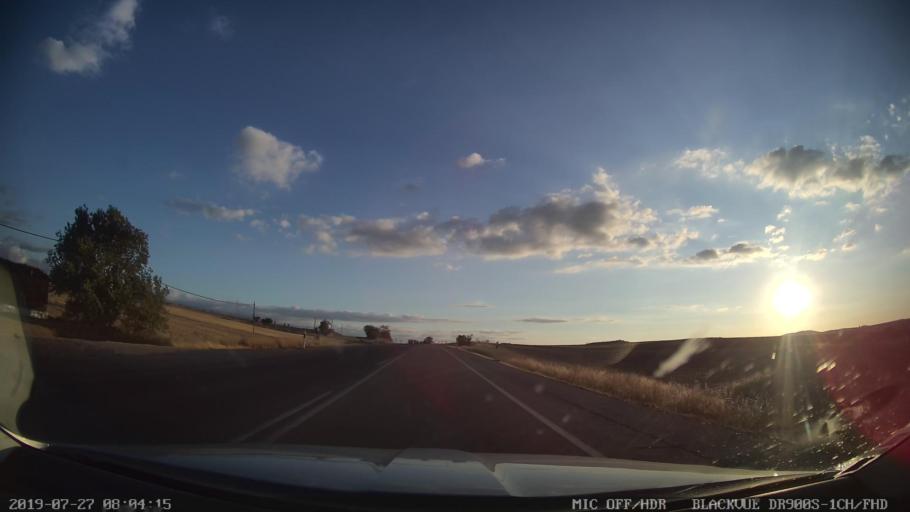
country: ES
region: Extremadura
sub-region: Provincia de Badajoz
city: Merida
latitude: 38.9333
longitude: -6.3113
